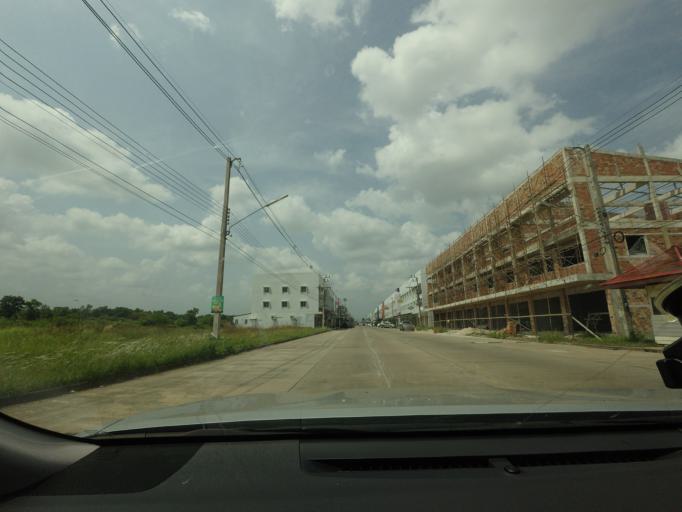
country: TH
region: Nakhon Si Thammarat
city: Nakhon Si Thammarat
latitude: 8.4301
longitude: 99.9840
